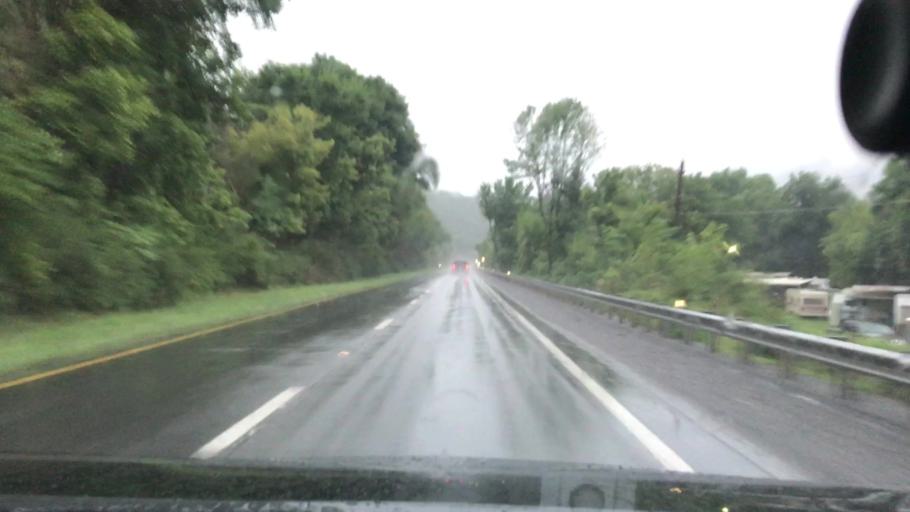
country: US
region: Virginia
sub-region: Giles County
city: Narrows
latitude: 37.3779
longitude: -80.8223
